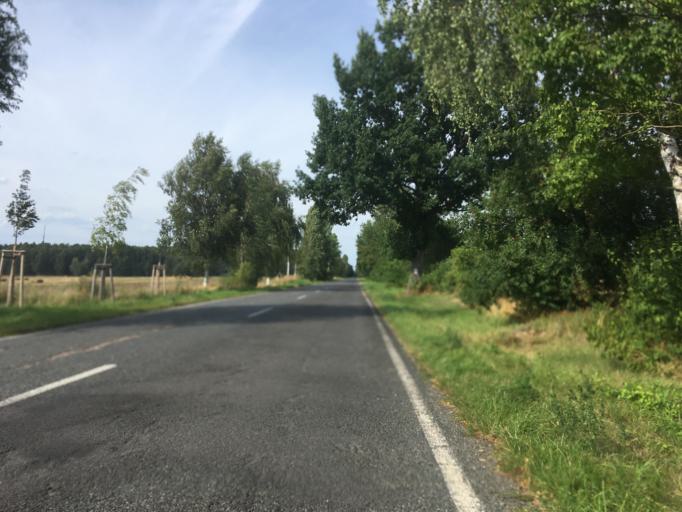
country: DE
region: Brandenburg
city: Biesenthal
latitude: 52.7702
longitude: 13.6512
